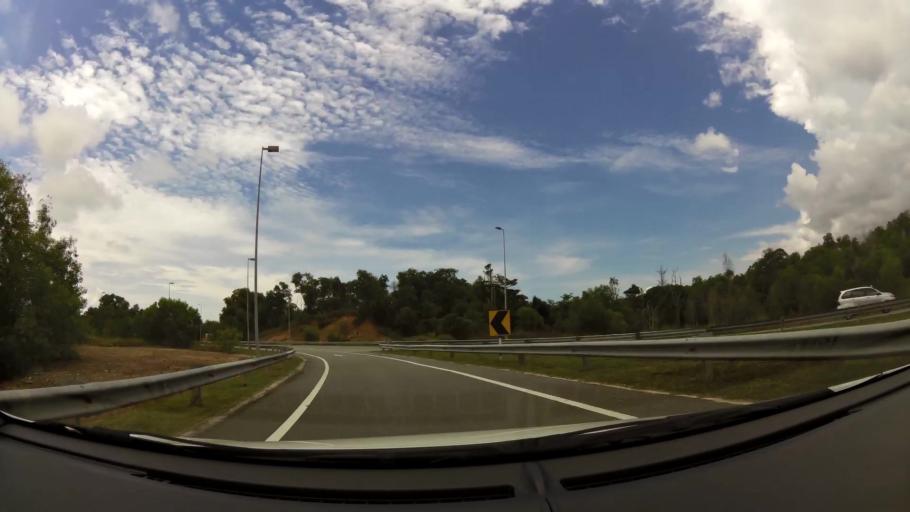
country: BN
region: Brunei and Muara
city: Bandar Seri Begawan
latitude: 4.9677
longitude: 114.8872
